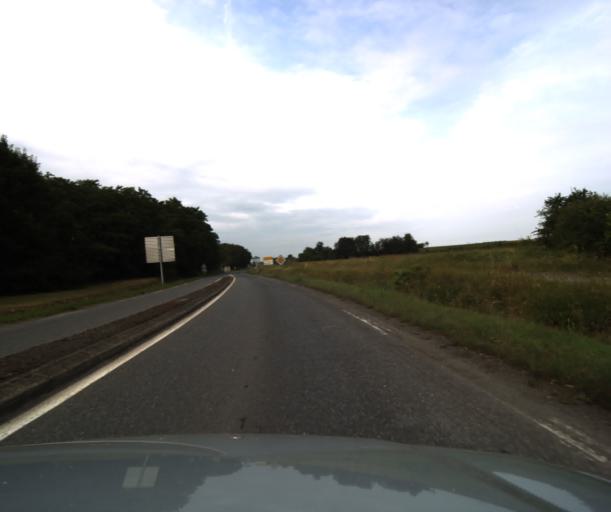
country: FR
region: Midi-Pyrenees
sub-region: Departement des Hautes-Pyrenees
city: Juillan
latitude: 43.2230
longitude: 0.0248
